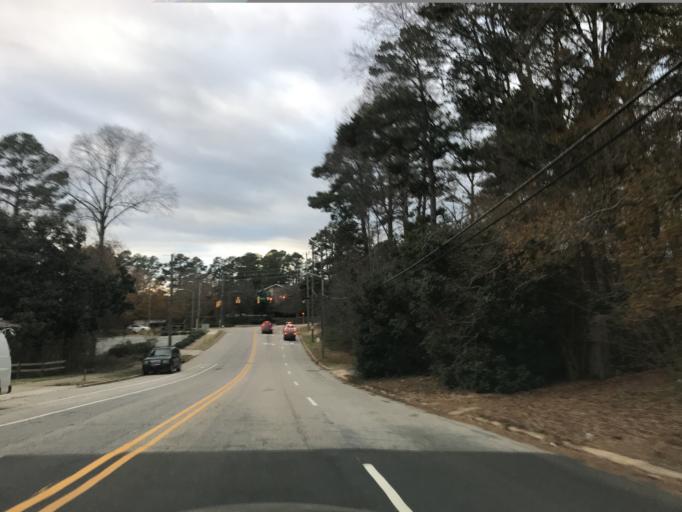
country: US
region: North Carolina
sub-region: Wake County
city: West Raleigh
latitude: 35.8398
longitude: -78.6720
